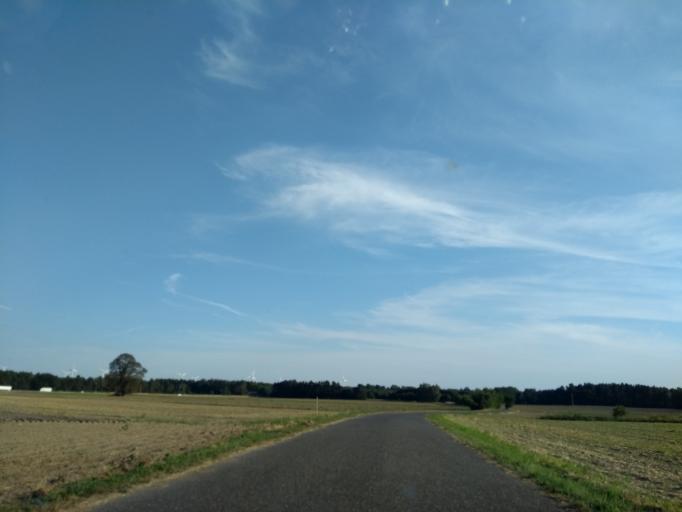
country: DE
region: Brandenburg
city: Lubbenau
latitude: 51.8456
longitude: 13.9162
